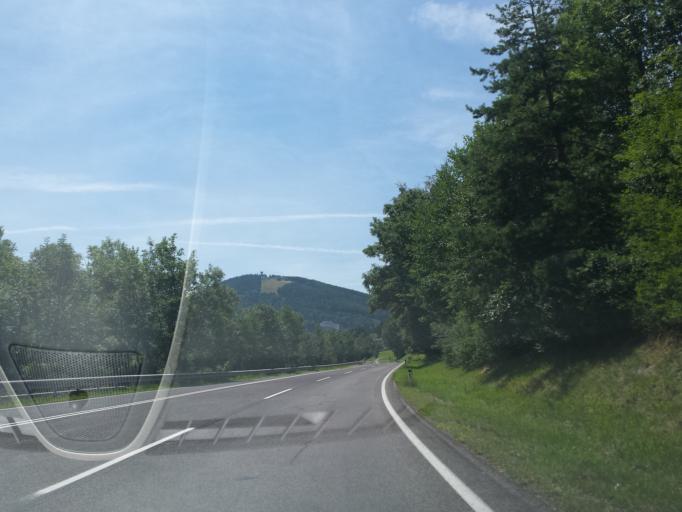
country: AT
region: Lower Austria
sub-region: Politischer Bezirk Neunkirchen
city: Semmering
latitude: 47.6441
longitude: 15.8498
